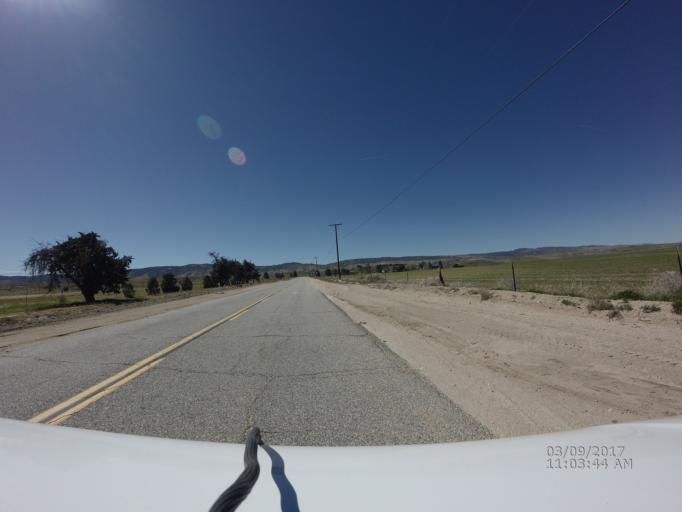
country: US
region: California
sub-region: Los Angeles County
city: Green Valley
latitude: 34.7122
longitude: -118.3527
